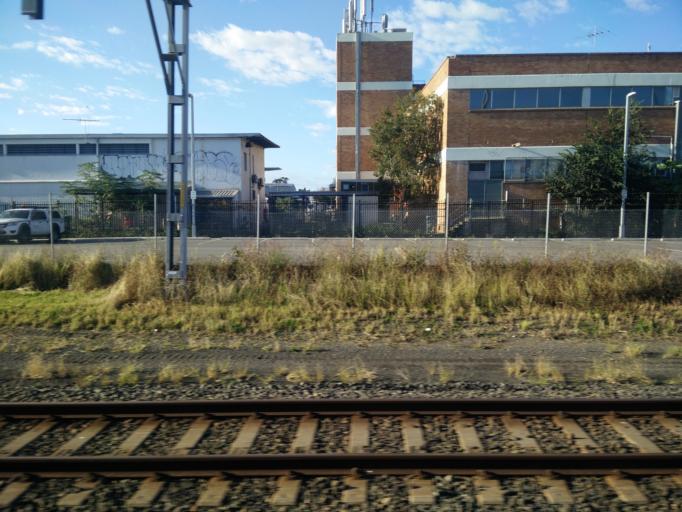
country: AU
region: New South Wales
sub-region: Marrickville
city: Newtown
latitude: -33.9122
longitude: 151.1701
